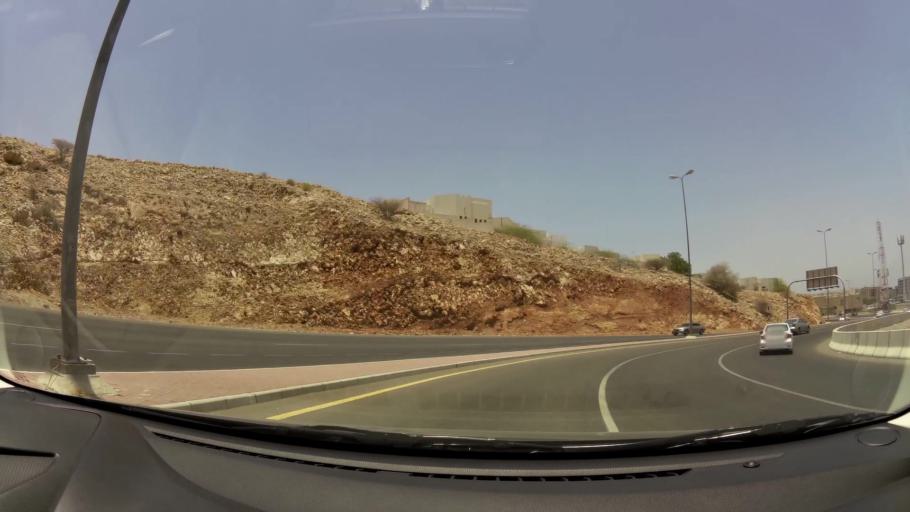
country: OM
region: Muhafazat Masqat
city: Bawshar
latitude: 23.6043
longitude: 58.4886
